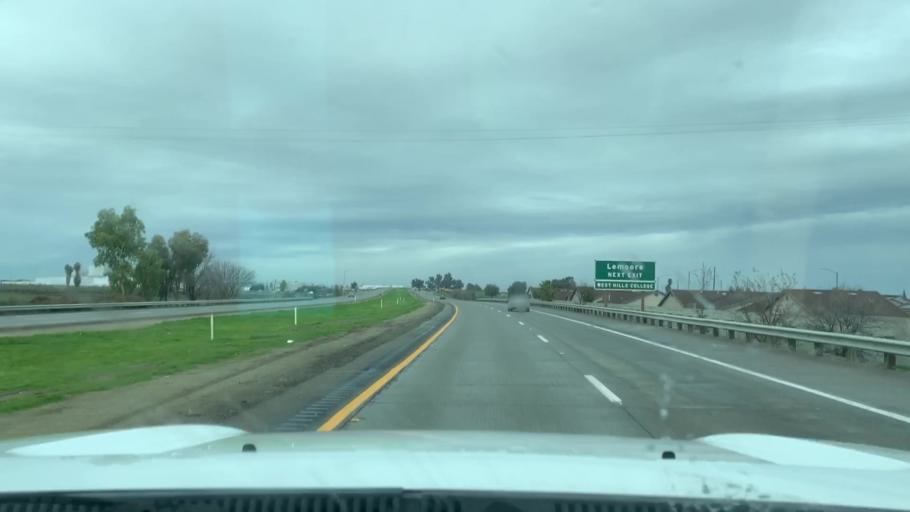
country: US
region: California
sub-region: Kings County
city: Lemoore
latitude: 36.2890
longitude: -119.8080
